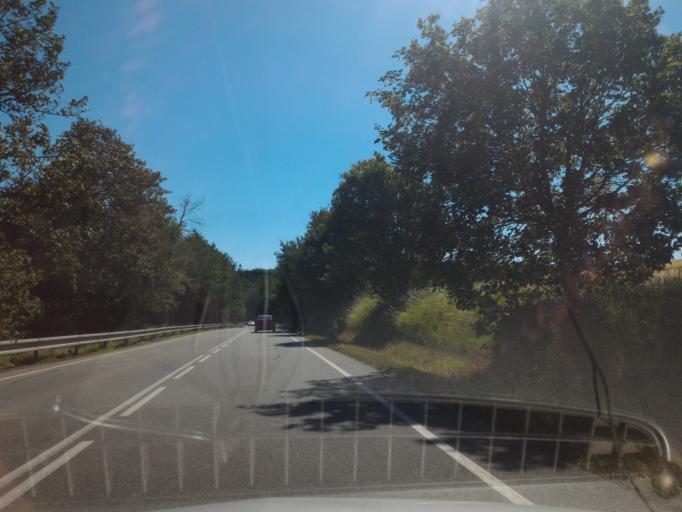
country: CZ
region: Vysocina
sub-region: Okres Jihlava
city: Trest'
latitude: 49.2624
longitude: 15.4742
